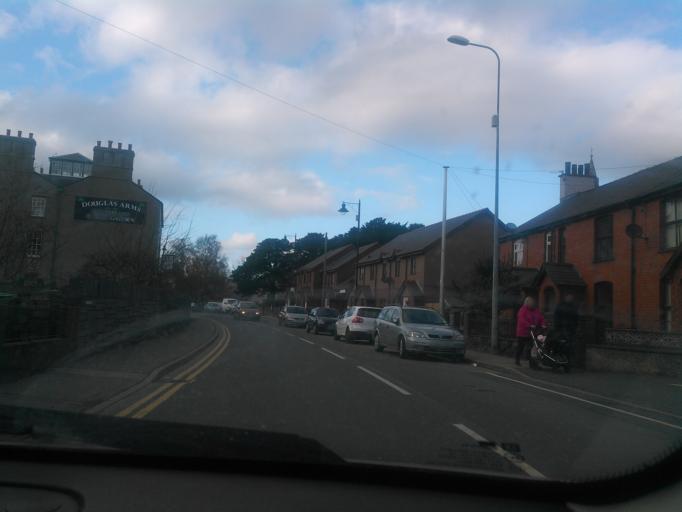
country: GB
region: Wales
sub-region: Gwynedd
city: Bethesda
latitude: 53.1785
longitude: -4.0583
